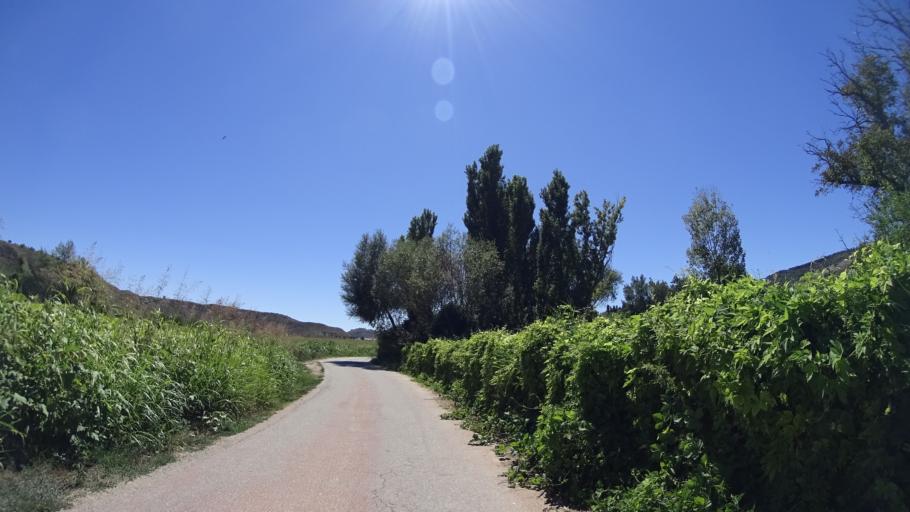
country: ES
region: Madrid
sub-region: Provincia de Madrid
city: Tielmes
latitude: 40.2391
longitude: -3.3151
